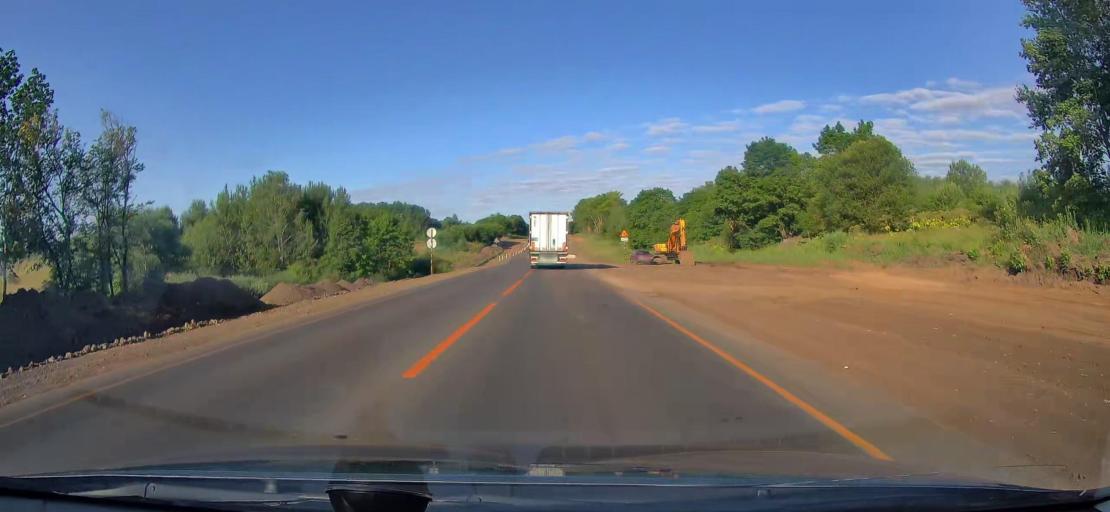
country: RU
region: Tula
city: Bol'shoye Skuratovo
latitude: 53.4492
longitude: 36.8504
